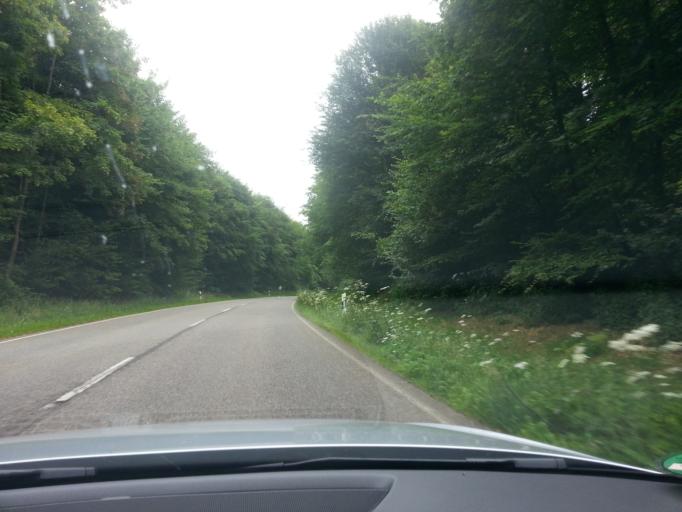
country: DE
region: Saarland
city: Perl
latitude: 49.4917
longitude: 6.4458
